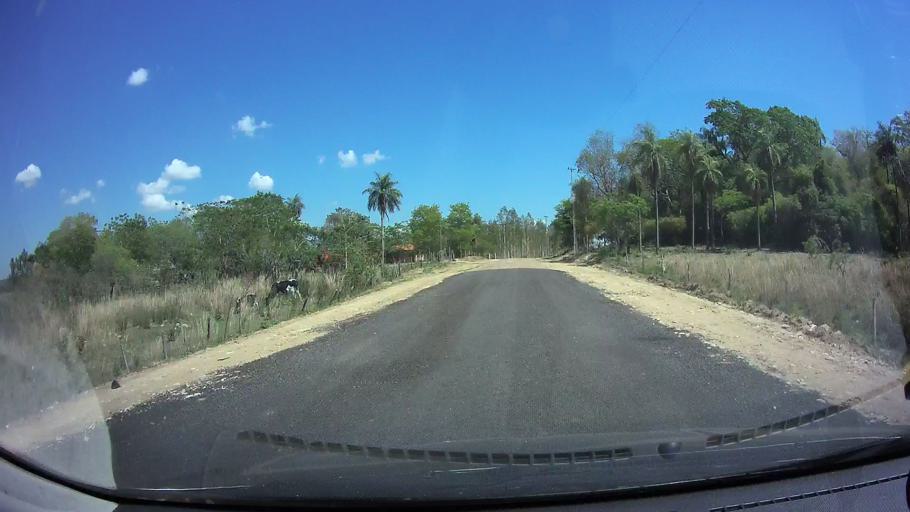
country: PY
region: Cordillera
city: Emboscada
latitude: -25.1401
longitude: -57.2646
